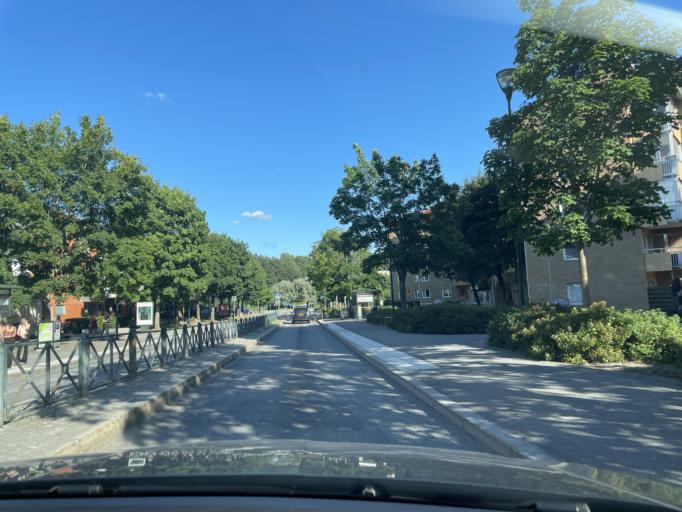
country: SE
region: Stockholm
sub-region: Sigtuna Kommun
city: Marsta
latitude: 59.6198
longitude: 17.8541
